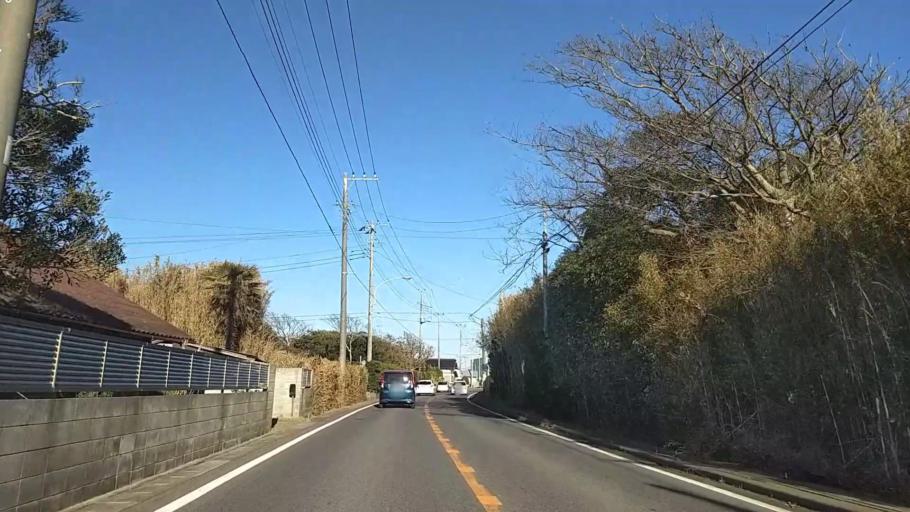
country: JP
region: Chiba
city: Yokaichiba
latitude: 35.6499
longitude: 140.5849
